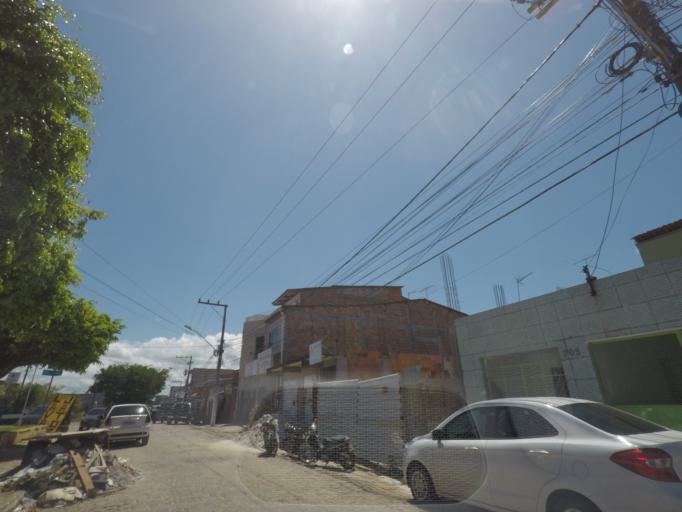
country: BR
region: Bahia
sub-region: Valenca
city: Valenca
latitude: -13.3604
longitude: -39.0669
